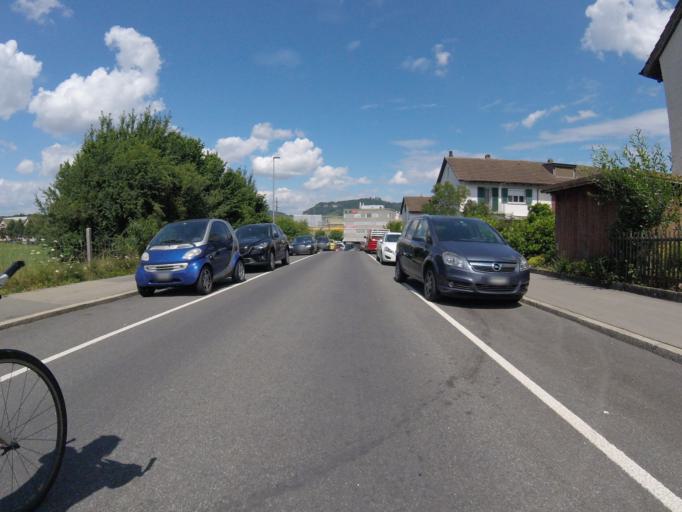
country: CH
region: Bern
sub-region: Bern-Mittelland District
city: Bolligen
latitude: 46.9594
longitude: 7.4783
